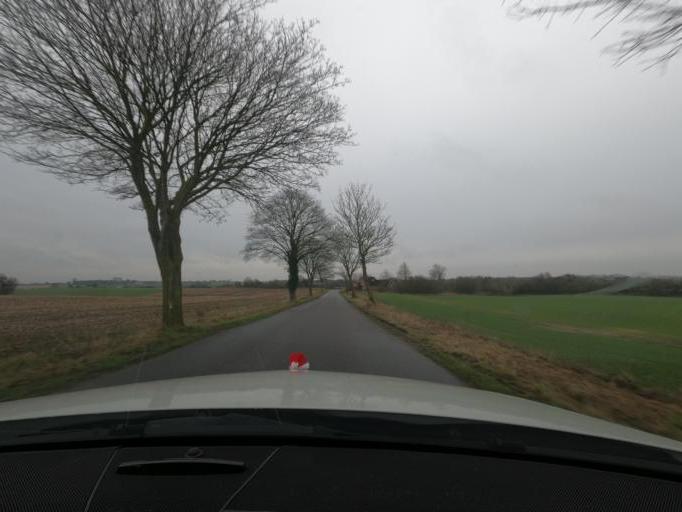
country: DK
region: South Denmark
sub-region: Haderslev Kommune
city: Haderslev
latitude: 55.1935
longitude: 9.4892
